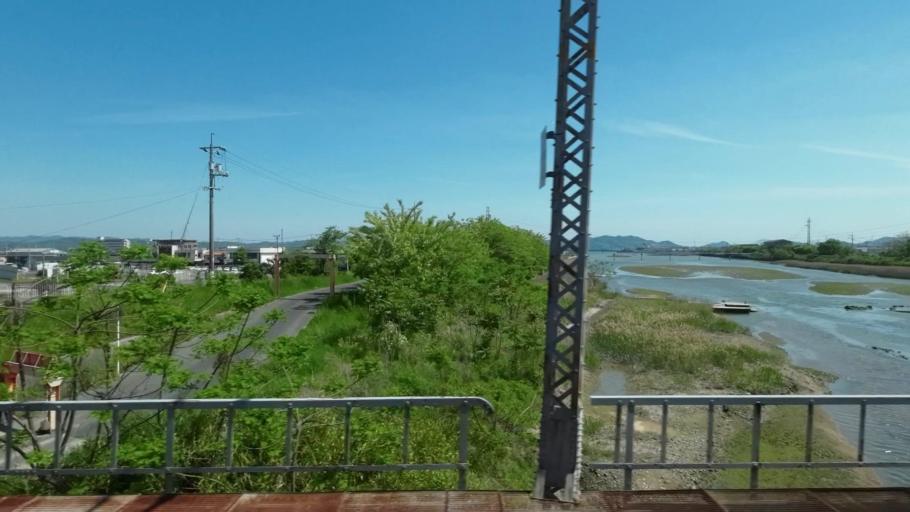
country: JP
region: Hiroshima
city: Onomichi
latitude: 34.4422
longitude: 133.2418
